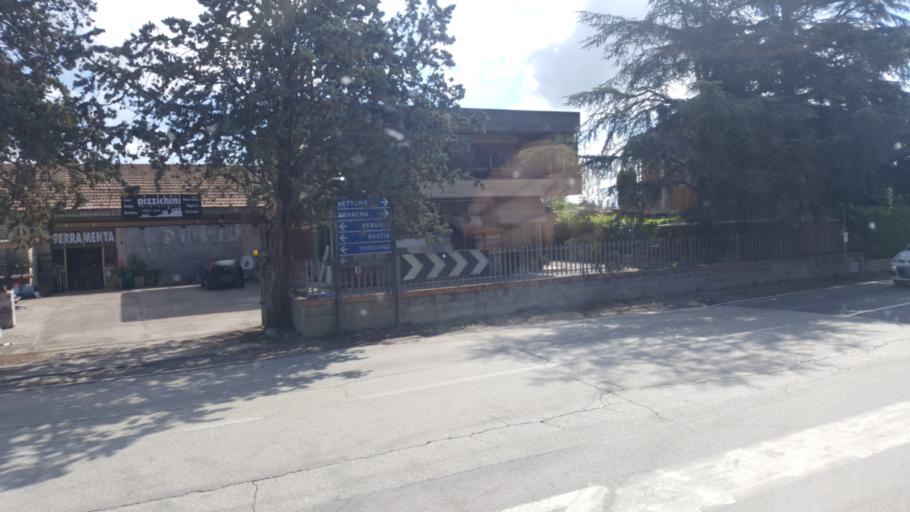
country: IT
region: Umbria
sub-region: Provincia di Perugia
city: Torgiano
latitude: 43.0240
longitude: 12.4471
